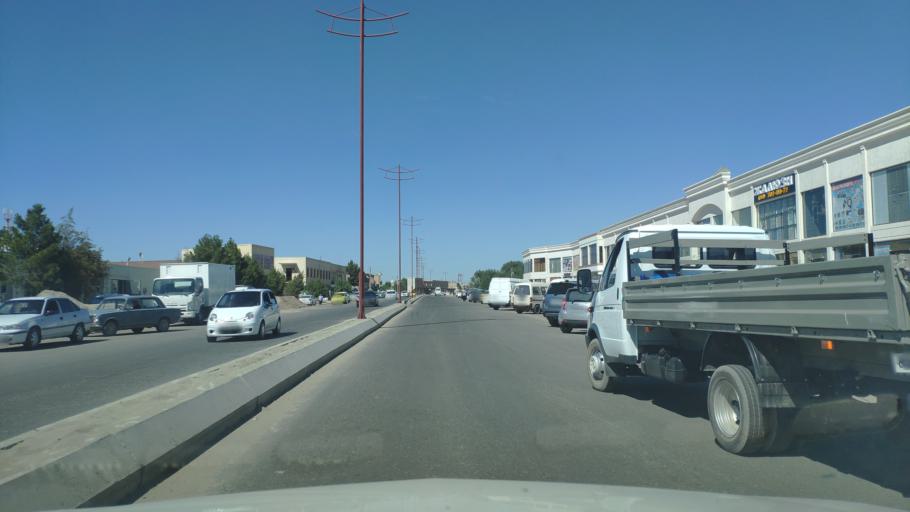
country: UZ
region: Bukhara
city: Bukhara
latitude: 39.7765
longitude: 64.3914
